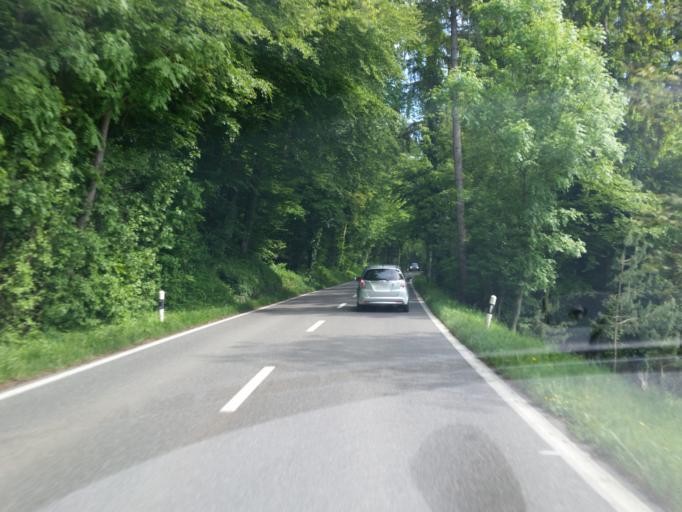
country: CH
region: Aargau
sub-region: Bezirk Bremgarten
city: Unterlunkhofen
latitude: 47.3270
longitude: 8.3815
